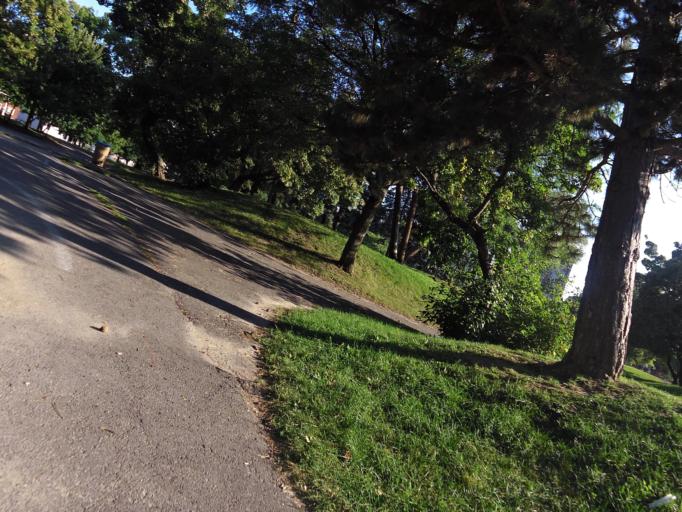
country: CA
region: Ontario
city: Ottawa
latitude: 45.4312
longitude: -75.7157
